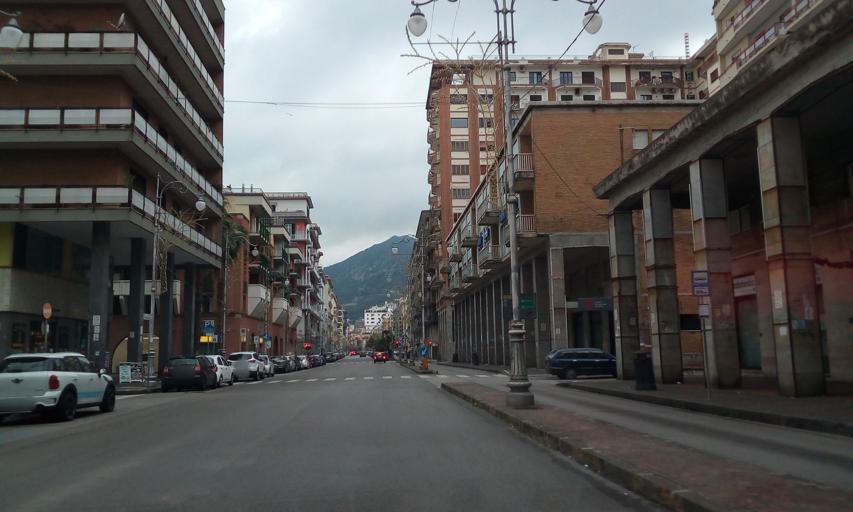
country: IT
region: Campania
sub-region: Provincia di Salerno
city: Salerno
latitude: 40.6751
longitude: 14.7701
